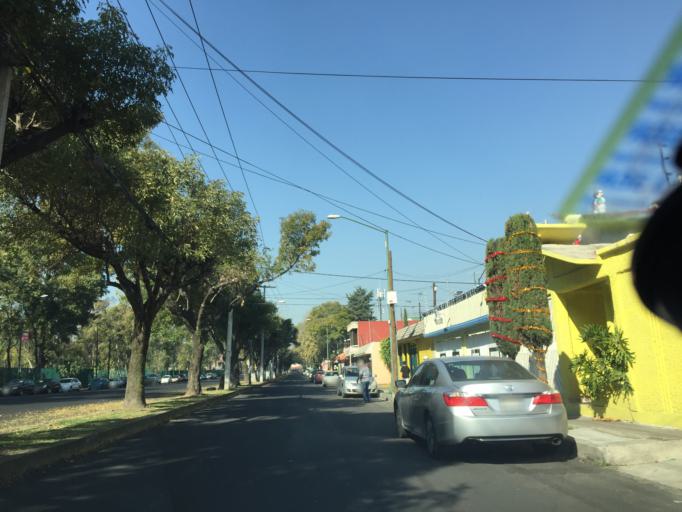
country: MX
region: Mexico
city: Vista Hermosa
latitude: 19.5014
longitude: -99.2086
